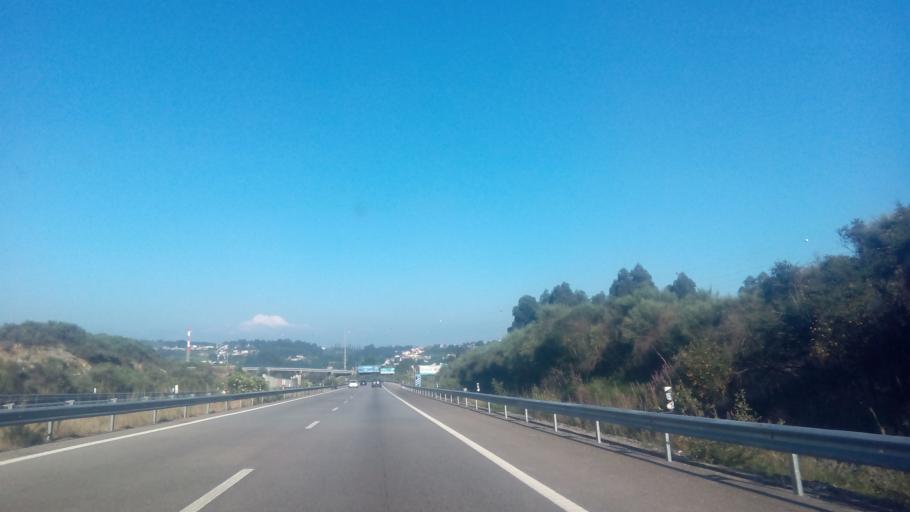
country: PT
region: Porto
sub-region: Pacos de Ferreira
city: Frazao
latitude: 41.2550
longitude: -8.4140
